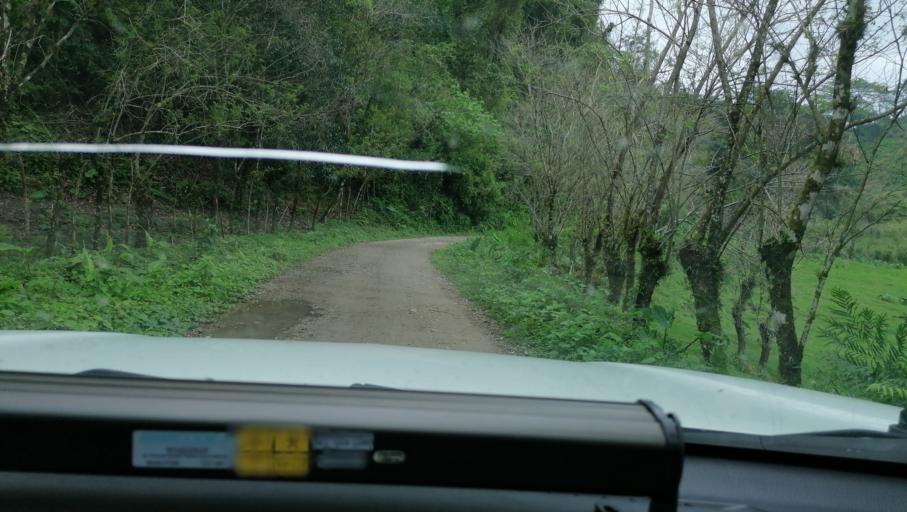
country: MX
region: Chiapas
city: Ixtacomitan
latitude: 17.3530
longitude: -93.1488
